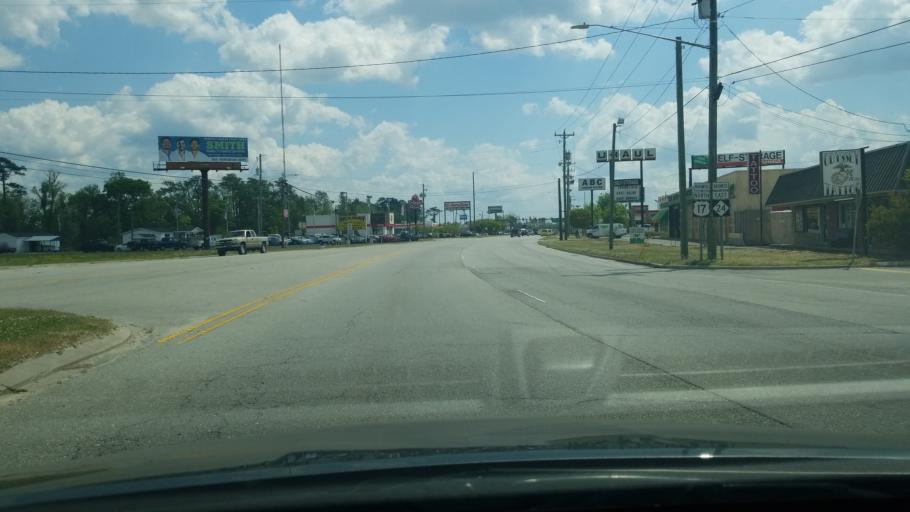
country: US
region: North Carolina
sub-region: Onslow County
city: Jacksonville
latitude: 34.7521
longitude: -77.4494
